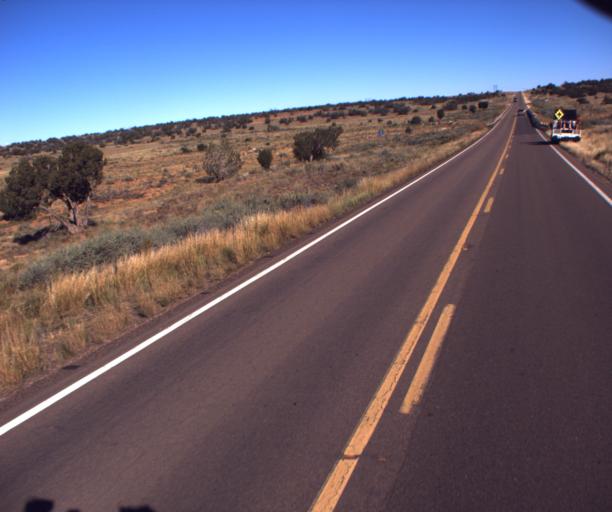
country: US
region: Arizona
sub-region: Navajo County
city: Snowflake
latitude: 34.6111
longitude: -110.0903
